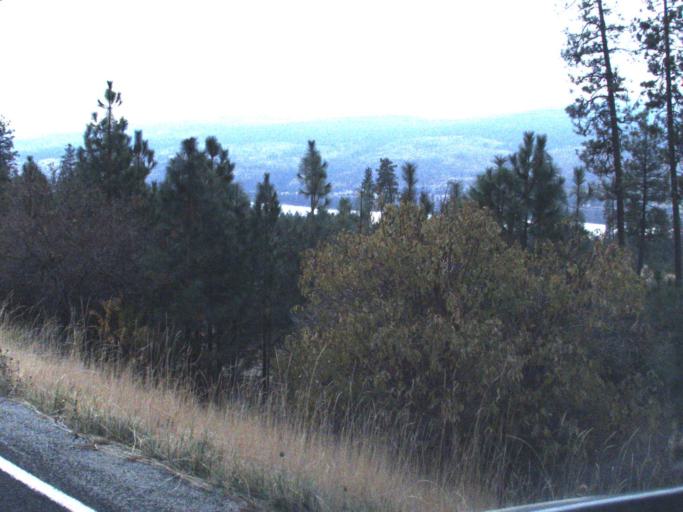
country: US
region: Washington
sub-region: Lincoln County
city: Davenport
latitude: 47.9401
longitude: -118.3164
